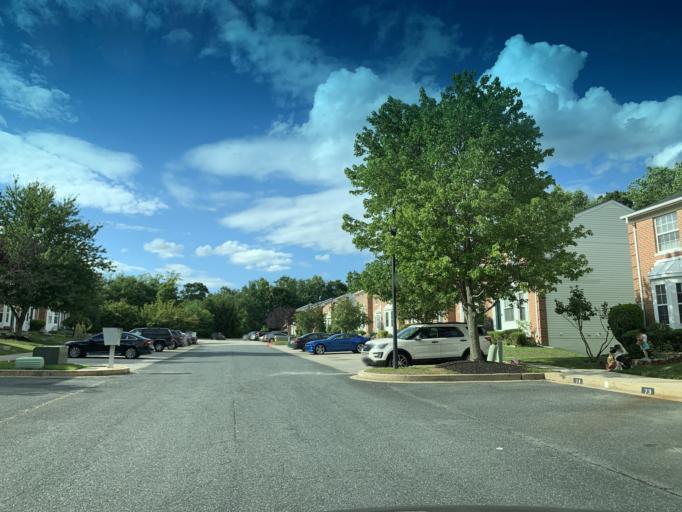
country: US
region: Maryland
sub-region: Harford County
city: Riverside
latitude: 39.4831
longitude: -76.2415
